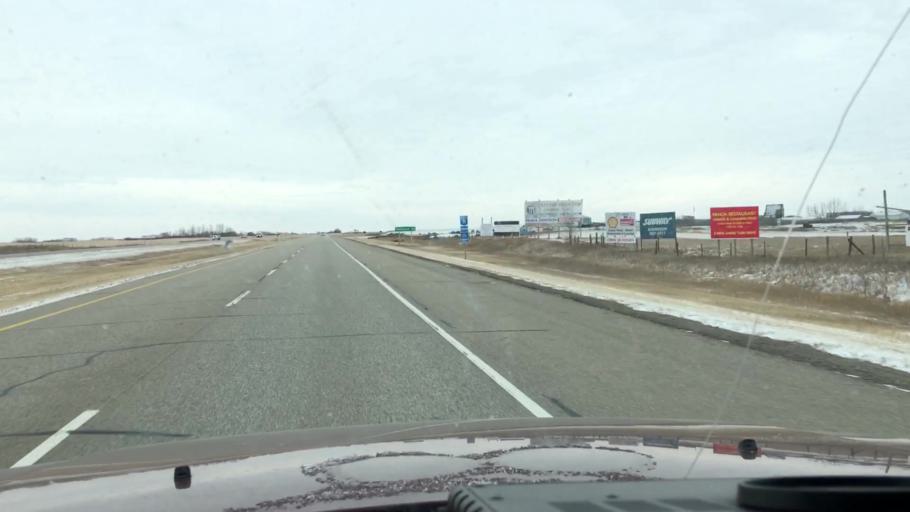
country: CA
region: Saskatchewan
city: Watrous
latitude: 51.3681
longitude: -106.1342
